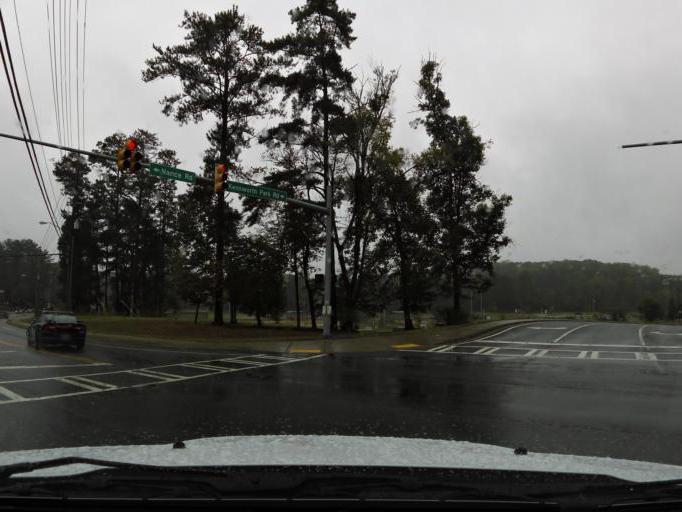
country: US
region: Georgia
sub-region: Cobb County
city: Acworth
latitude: 34.0489
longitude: -84.6622
